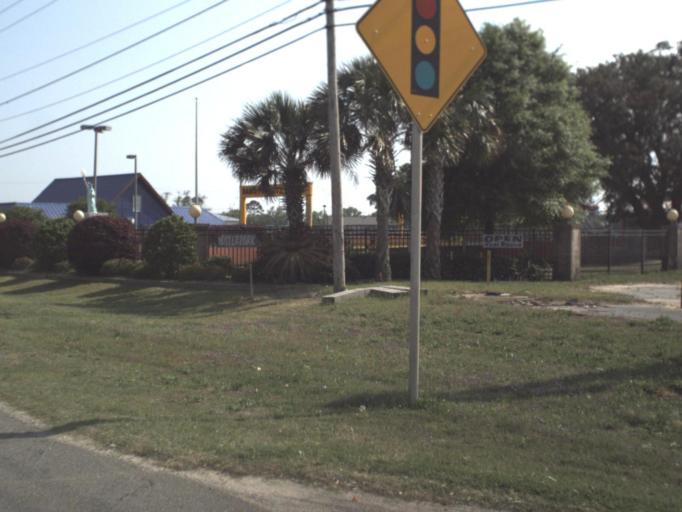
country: US
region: Florida
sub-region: Escambia County
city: Ensley
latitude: 30.4899
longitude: -87.2603
